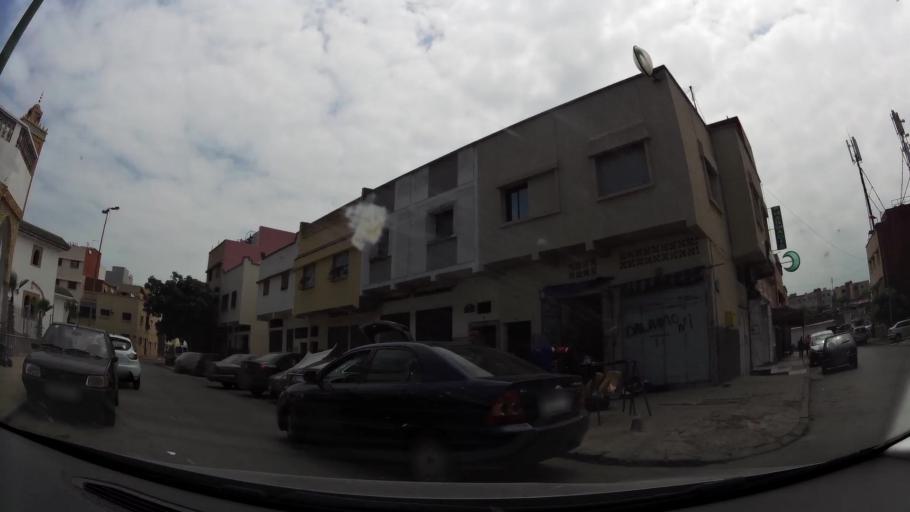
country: MA
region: Rabat-Sale-Zemmour-Zaer
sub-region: Skhirate-Temara
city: Temara
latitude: 33.9821
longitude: -6.8916
